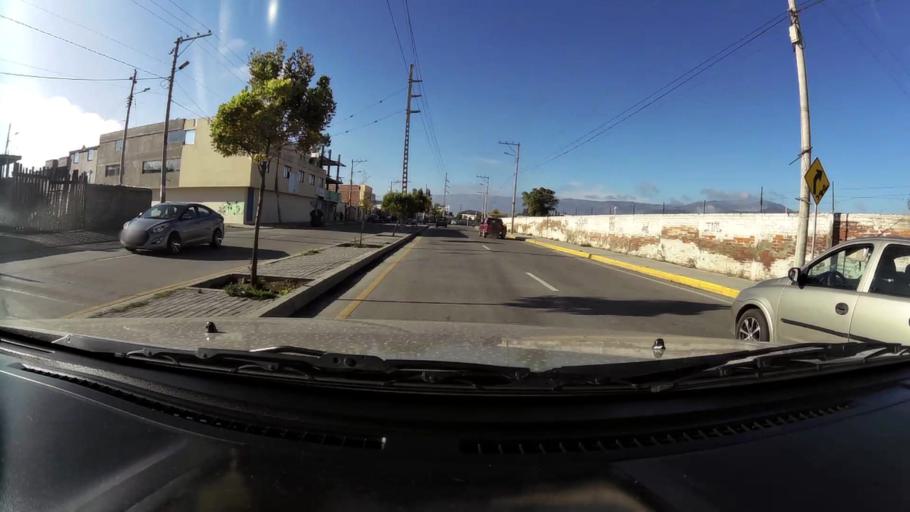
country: EC
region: Chimborazo
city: Riobamba
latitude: -1.6873
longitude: -78.6307
